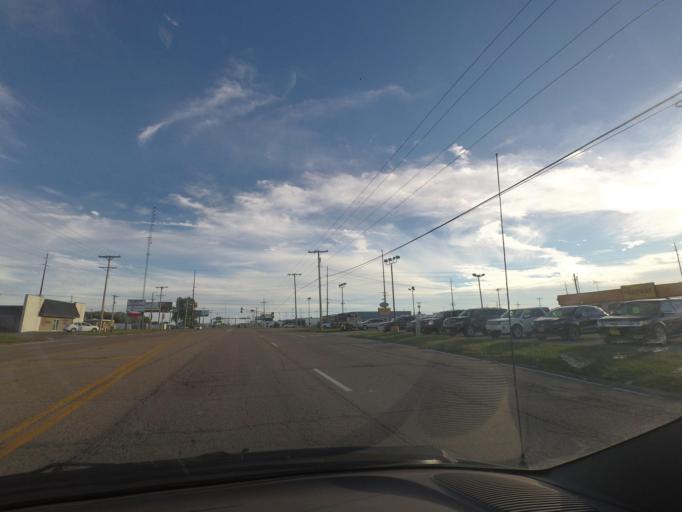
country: US
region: Illinois
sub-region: Sangamon County
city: Grandview
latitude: 39.7959
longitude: -89.6060
